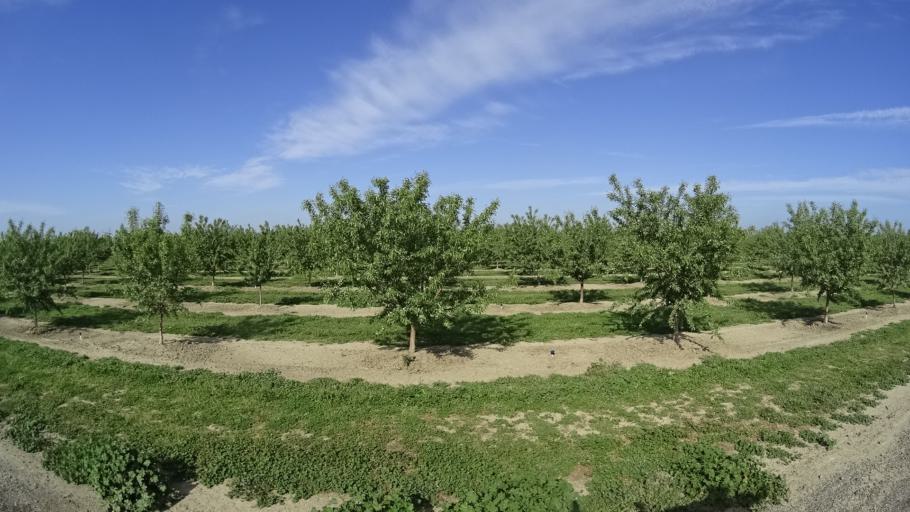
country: US
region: California
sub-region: Glenn County
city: Hamilton City
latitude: 39.6250
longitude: -122.0463
